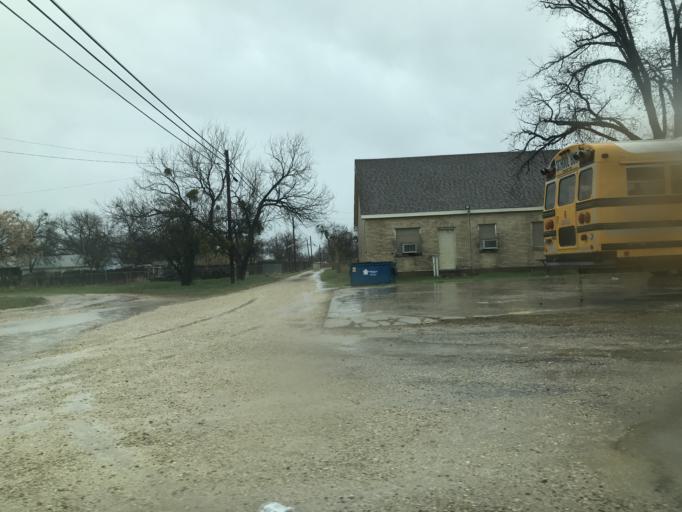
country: US
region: Texas
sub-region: Tom Green County
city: San Angelo
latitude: 31.4673
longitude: -100.4188
